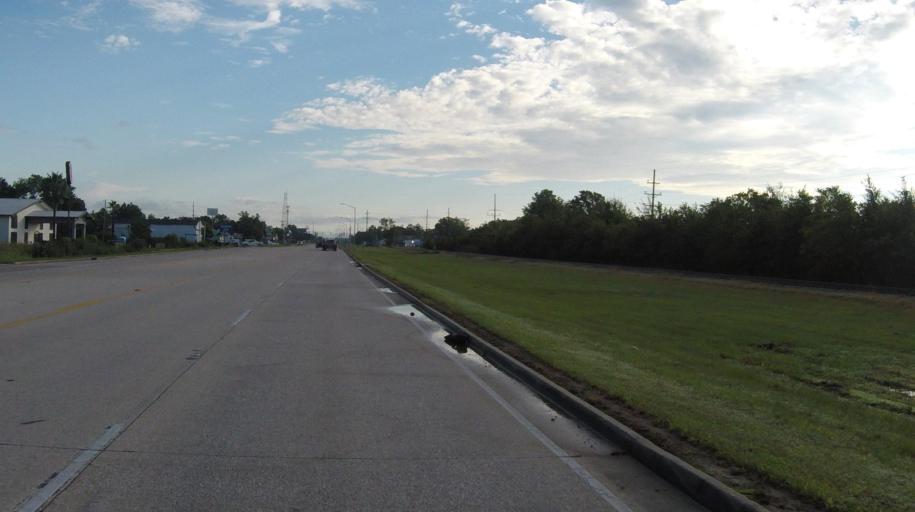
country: US
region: Louisiana
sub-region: Allen Parish
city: Kinder
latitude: 30.4792
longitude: -92.8535
